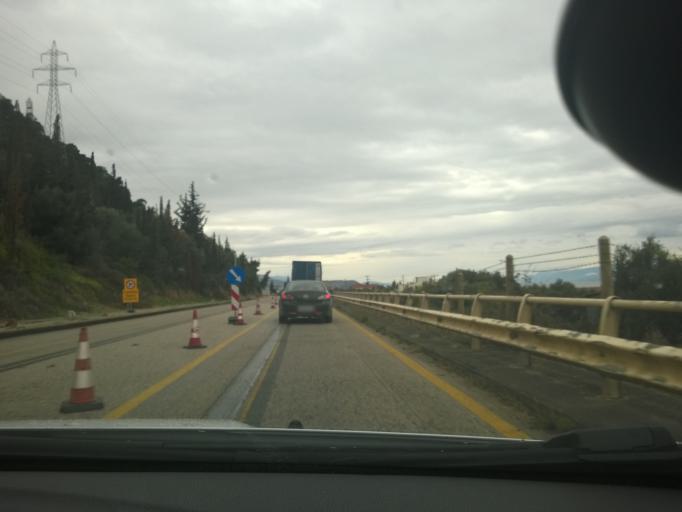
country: GR
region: West Greece
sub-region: Nomos Achaias
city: Aiyira
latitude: 38.1333
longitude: 22.4347
